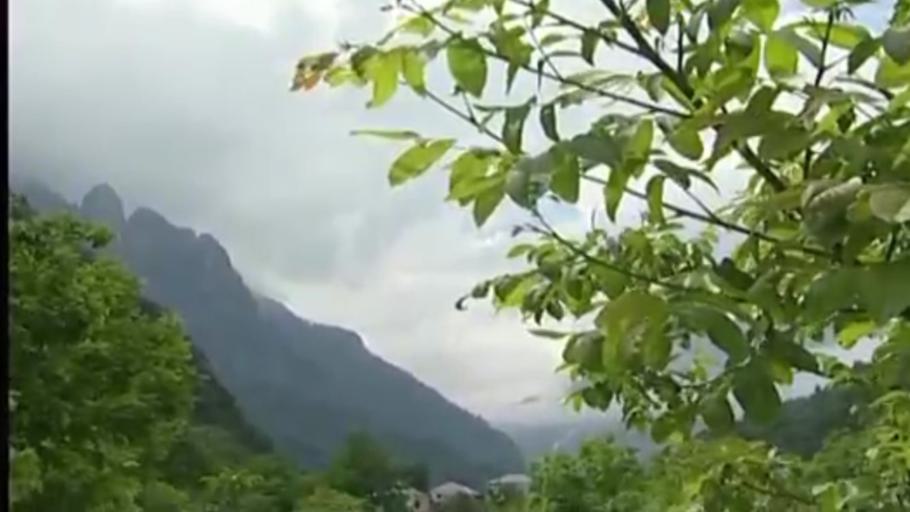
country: AL
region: Kukes
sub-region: Rrethi i Tropojes
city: Valbone
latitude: 42.4352
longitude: 19.9736
